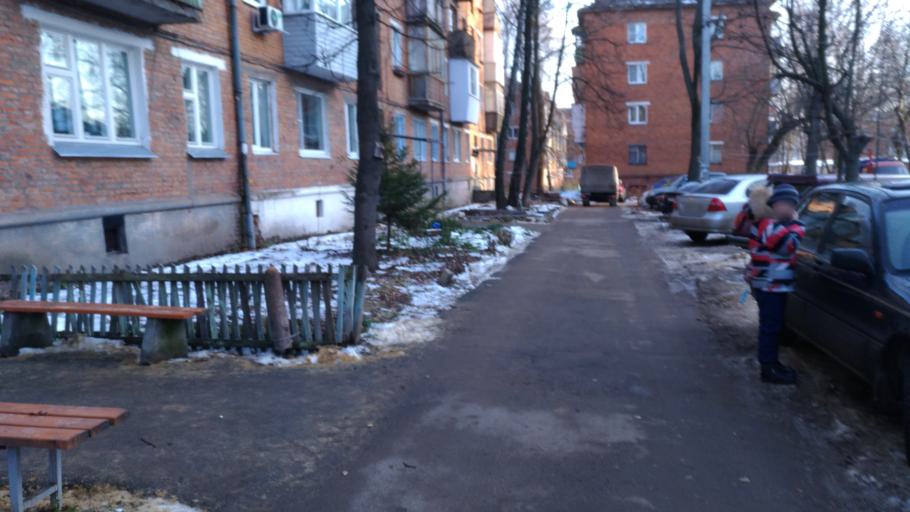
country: RU
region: Tula
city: Tula
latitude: 54.1901
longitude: 37.6972
